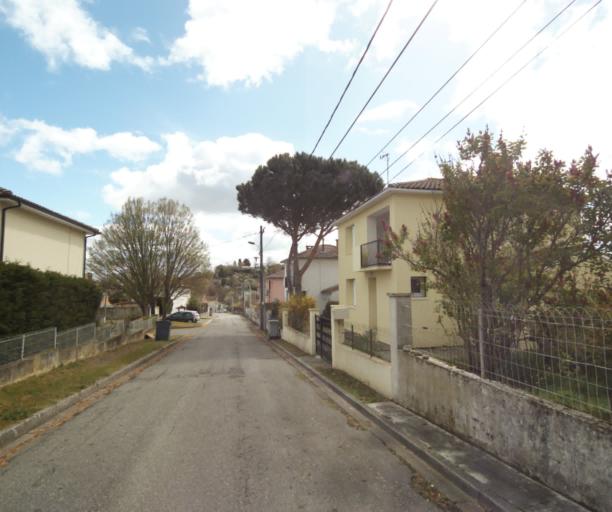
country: FR
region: Midi-Pyrenees
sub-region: Departement de l'Ariege
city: Saverdun
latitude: 43.2315
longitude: 1.5718
